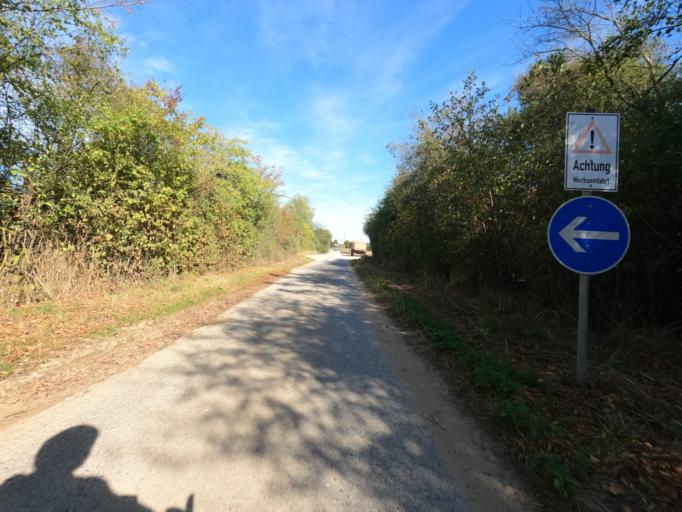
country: DE
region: North Rhine-Westphalia
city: Erkelenz
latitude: 51.0547
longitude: 6.3605
